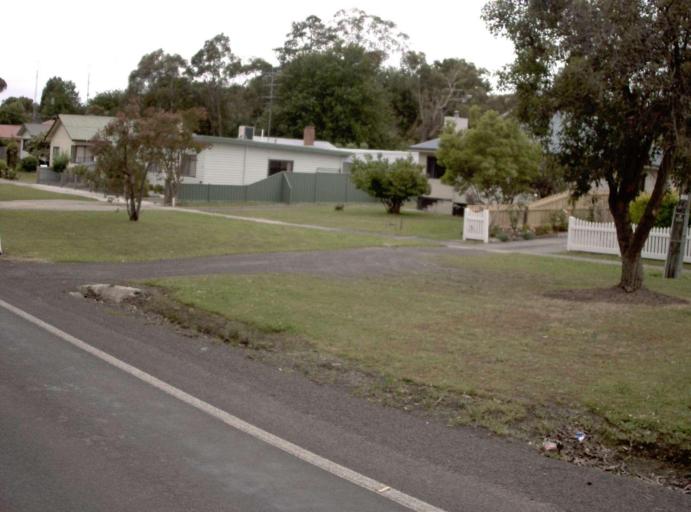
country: AU
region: Victoria
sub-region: Bass Coast
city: North Wonthaggi
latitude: -38.5806
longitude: 146.0093
